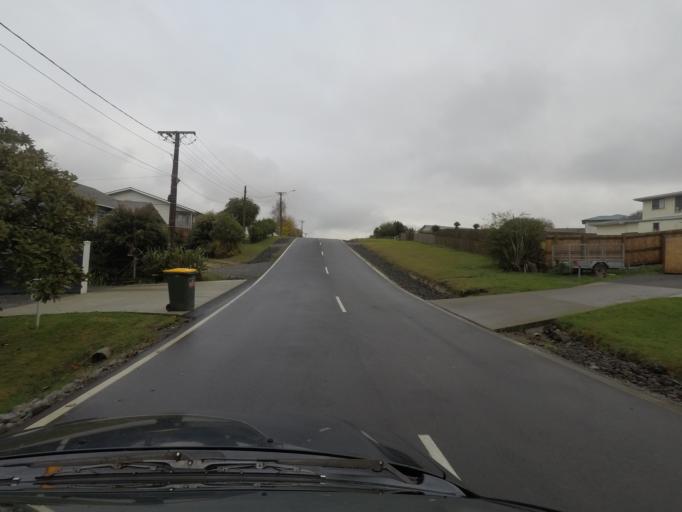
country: NZ
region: Auckland
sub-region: Auckland
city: Rosebank
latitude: -36.7600
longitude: 174.5947
